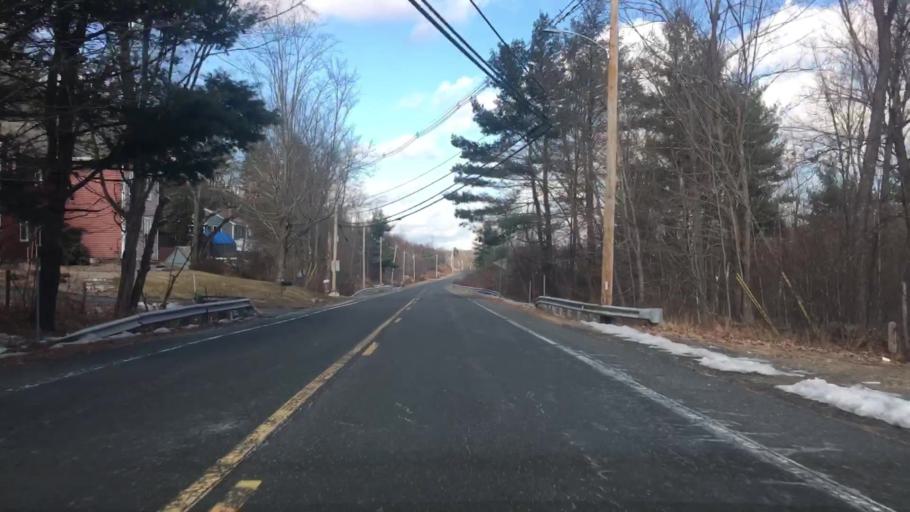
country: US
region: Massachusetts
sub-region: Hampden County
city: Brimfield
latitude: 42.1047
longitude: -72.2017
